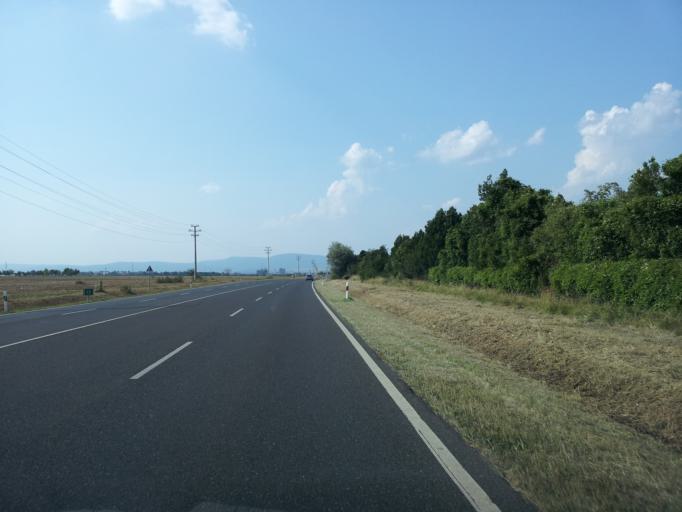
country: HU
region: Veszprem
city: Veszprem
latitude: 47.0660
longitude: 17.9220
